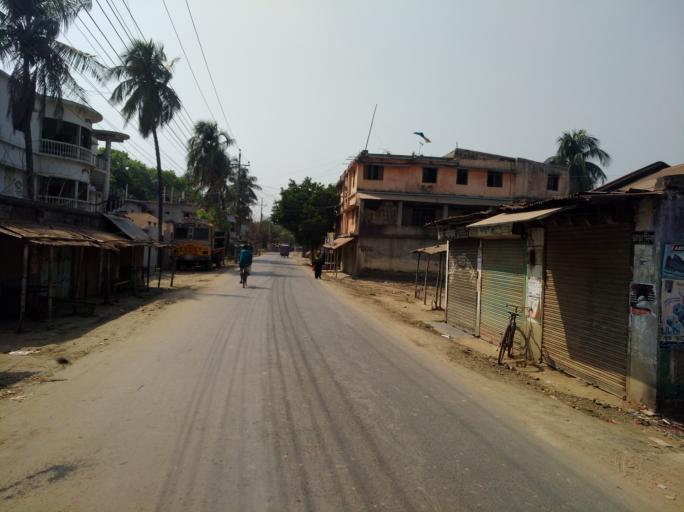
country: BD
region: Khulna
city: Kaliganj
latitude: 23.5501
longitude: 89.1664
